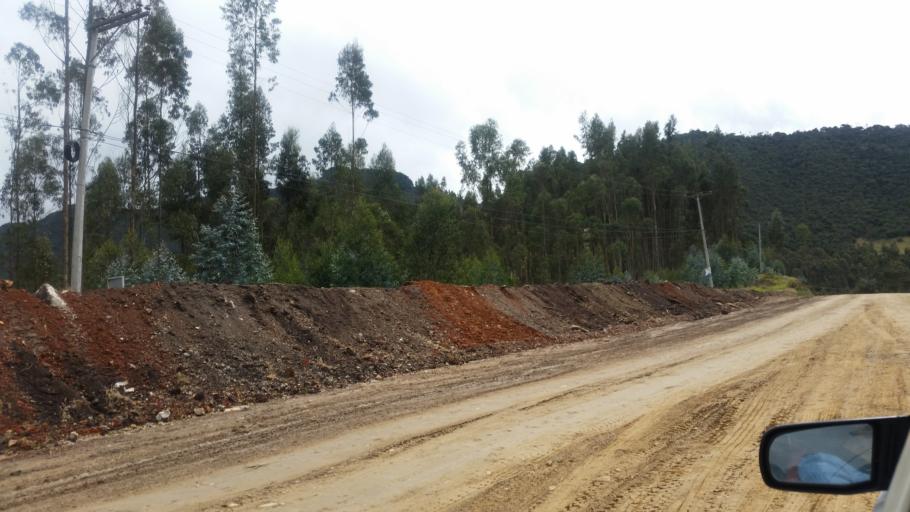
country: CO
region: Cundinamarca
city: La Calera
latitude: 4.7227
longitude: -73.9523
